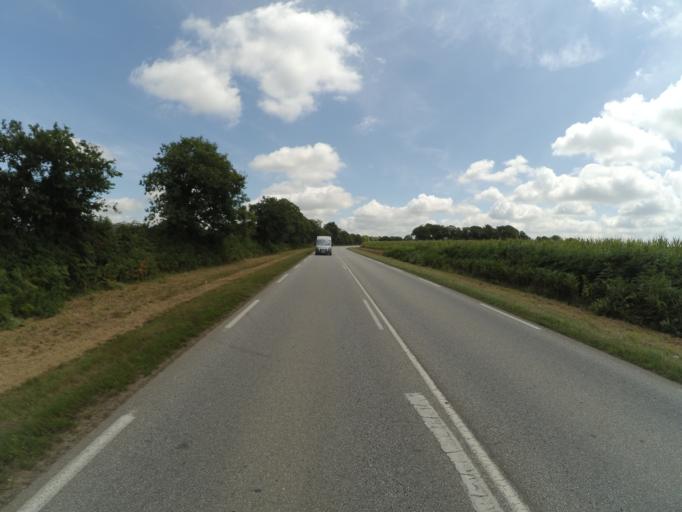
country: FR
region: Brittany
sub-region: Departement du Finistere
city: Saint-Yvi
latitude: 47.9698
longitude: -3.9593
